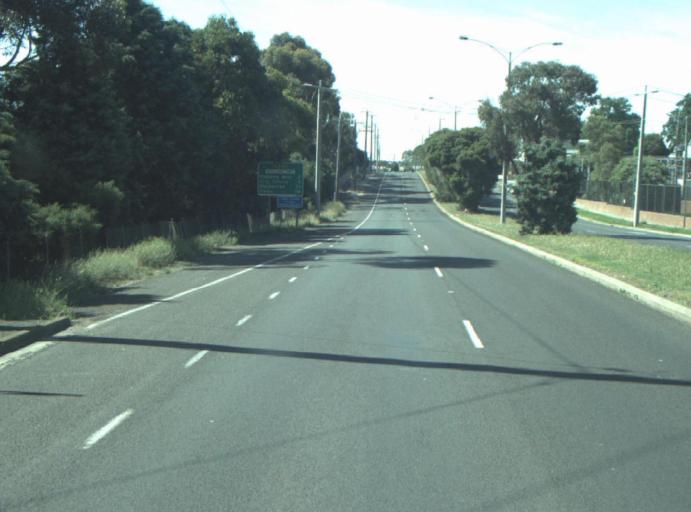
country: AU
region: Victoria
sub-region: Greater Geelong
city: Hamlyn Heights
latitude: -38.1276
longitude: 144.3401
